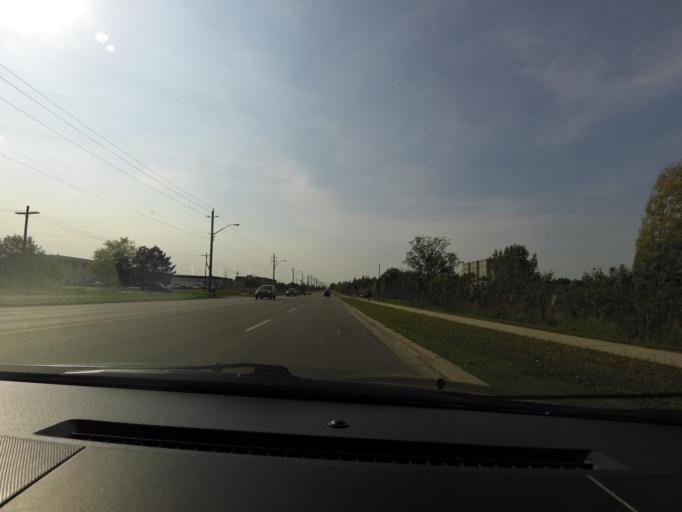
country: CA
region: Ontario
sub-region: Wellington County
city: Guelph
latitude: 43.5486
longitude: -80.2734
